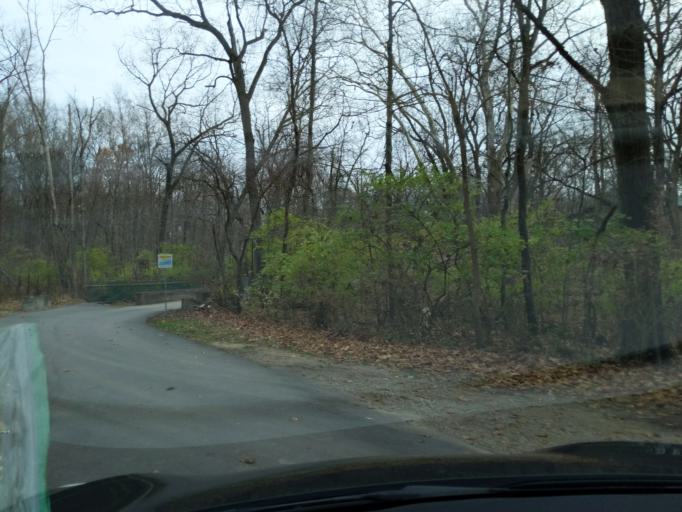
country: US
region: Indiana
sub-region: Saint Joseph County
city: Georgetown
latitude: 41.7289
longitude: -86.2634
